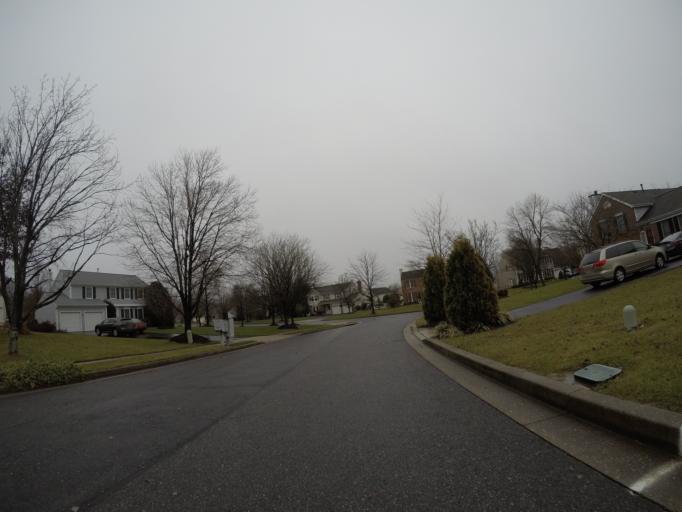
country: US
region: Maryland
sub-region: Howard County
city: Ellicott City
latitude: 39.2290
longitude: -76.7989
